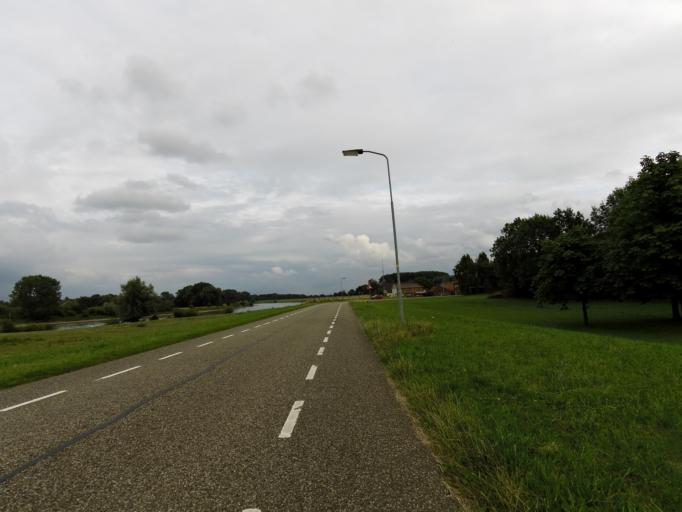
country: NL
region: Gelderland
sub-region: Gemeente Rheden
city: De Steeg
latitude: 51.9967
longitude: 6.0798
